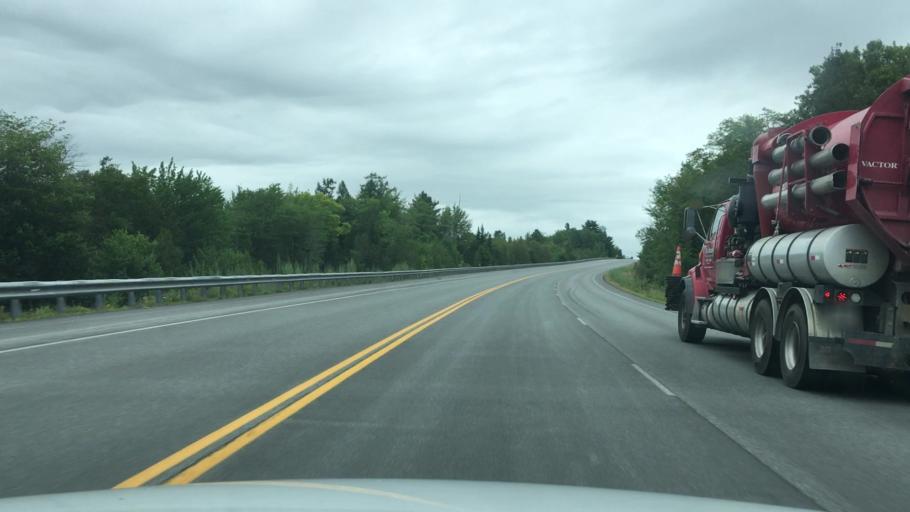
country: US
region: Maine
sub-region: Hancock County
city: Franklin
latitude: 44.8459
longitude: -68.3397
